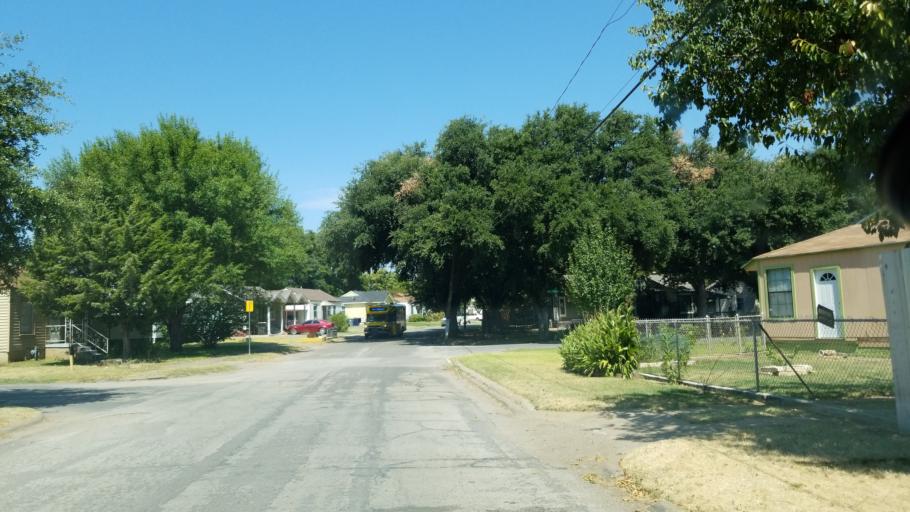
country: US
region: Texas
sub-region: Dallas County
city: Cockrell Hill
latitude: 32.7454
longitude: -96.8870
